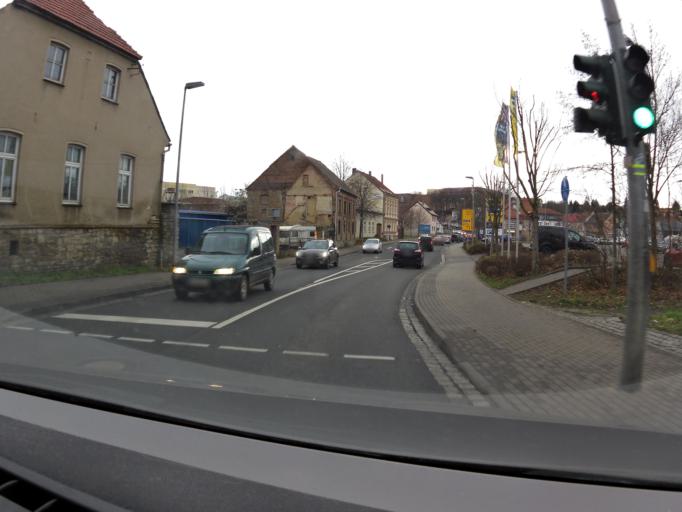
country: DE
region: Saxony-Anhalt
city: Aschersleben
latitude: 51.7506
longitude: 11.4603
